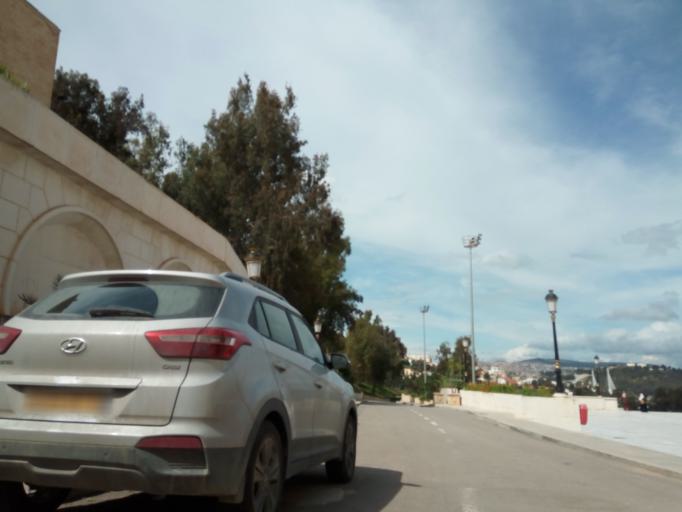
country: DZ
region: Constantine
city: Constantine
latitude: 36.3476
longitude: 6.6030
